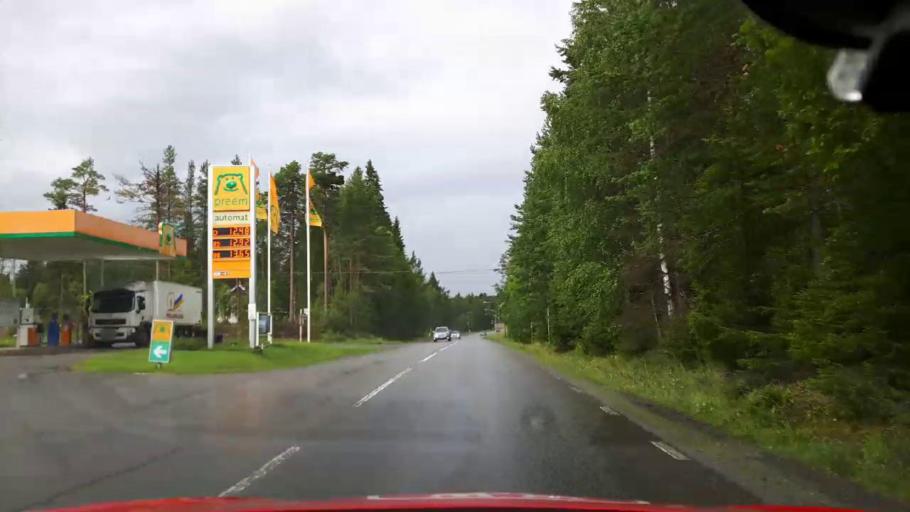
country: SE
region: Jaemtland
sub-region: Krokoms Kommun
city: Krokom
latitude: 63.3429
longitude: 14.2662
